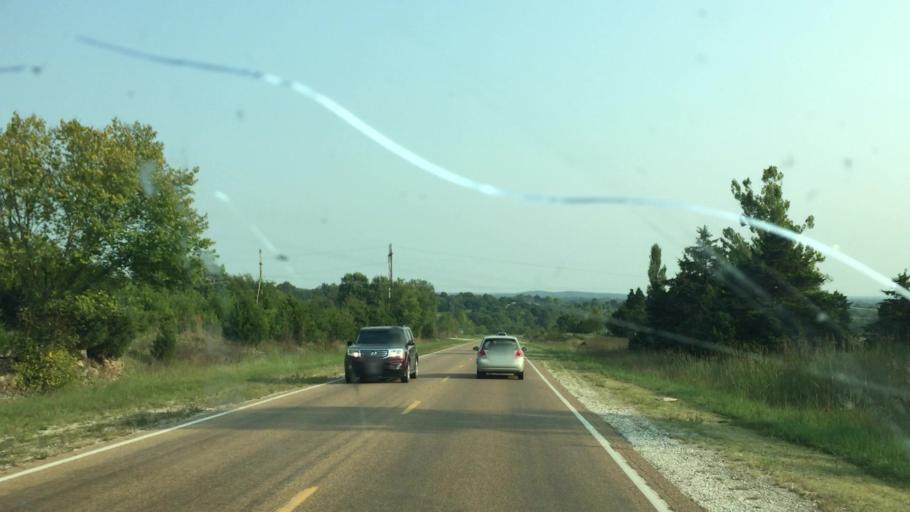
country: US
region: Missouri
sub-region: Pulaski County
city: Richland
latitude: 37.8410
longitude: -92.4093
